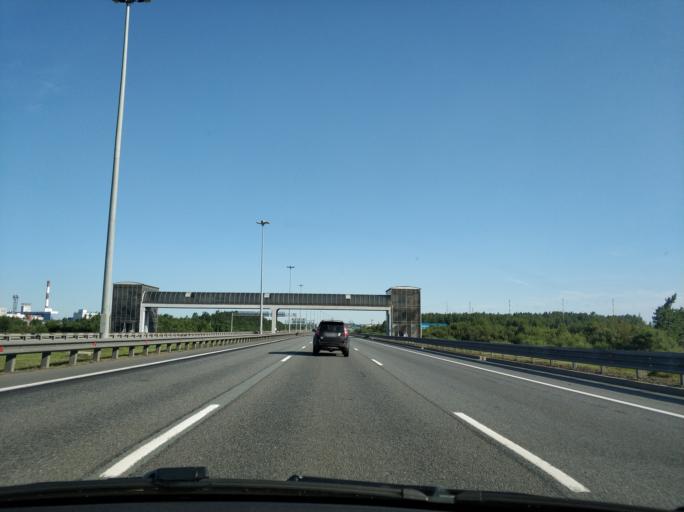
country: RU
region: Leningrad
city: Bugry
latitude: 60.0670
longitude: 30.3847
